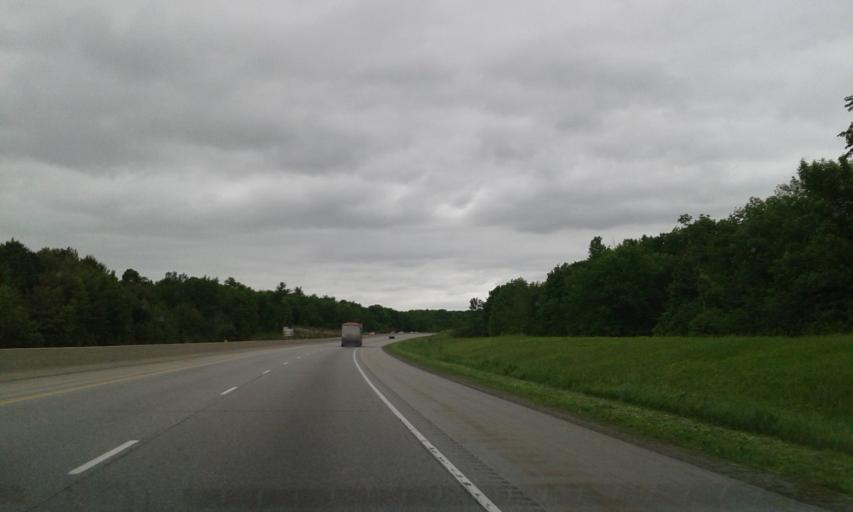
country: CA
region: Ontario
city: Brockville
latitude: 44.5412
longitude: -75.7681
